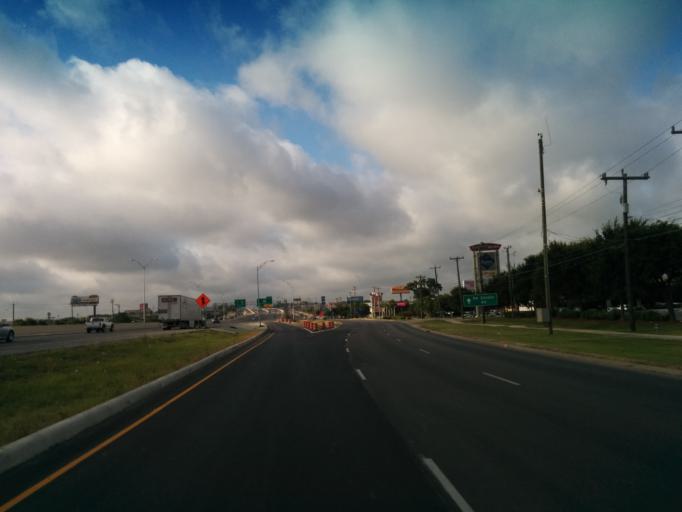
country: US
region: Texas
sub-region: Bexar County
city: Shavano Park
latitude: 29.5688
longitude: -98.5931
